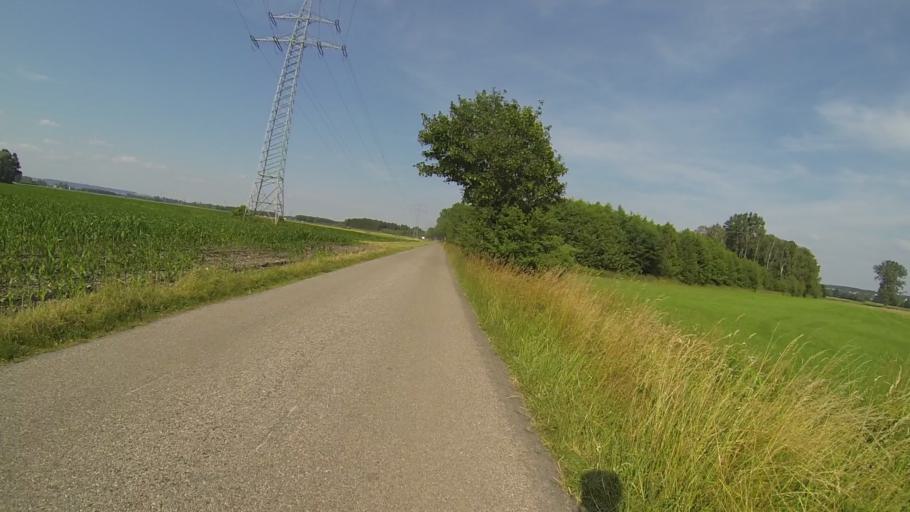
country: DE
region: Bavaria
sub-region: Swabia
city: Neu-Ulm
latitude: 48.3732
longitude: 10.0472
